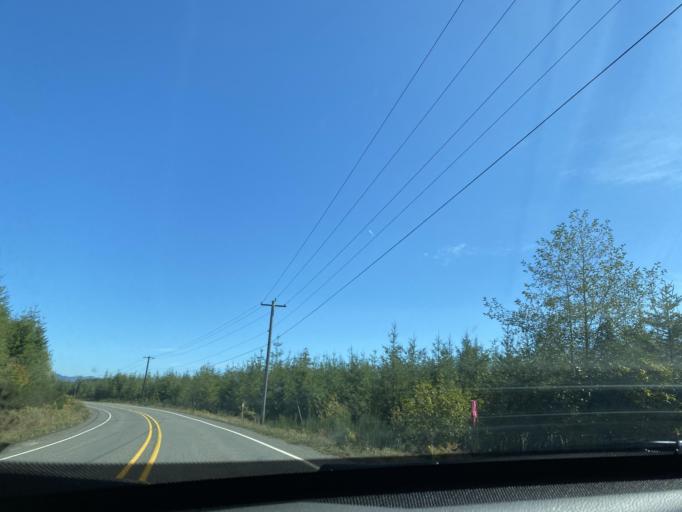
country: US
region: Washington
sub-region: Clallam County
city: Forks
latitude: 47.9626
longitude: -124.4277
